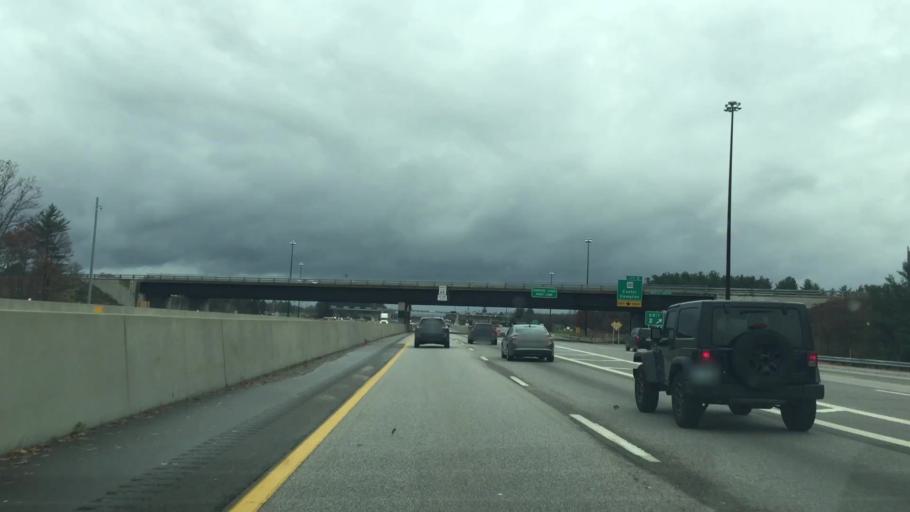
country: US
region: New Hampshire
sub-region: Rockingham County
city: Hampton
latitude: 42.9581
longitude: -70.8571
